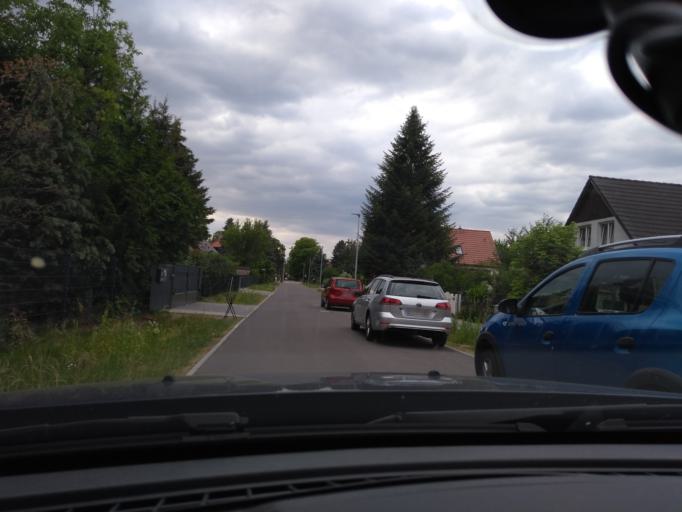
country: DE
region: Brandenburg
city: Falkensee
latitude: 52.5559
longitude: 13.0832
